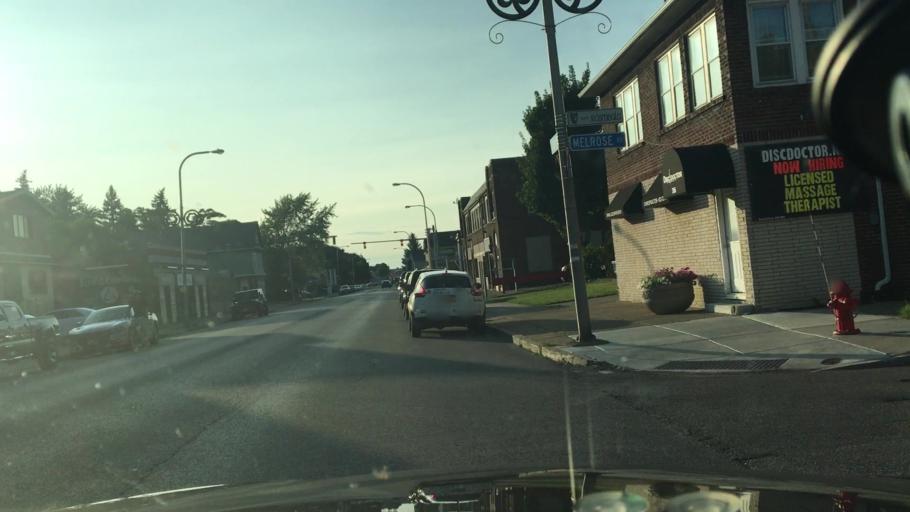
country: US
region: New York
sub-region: Erie County
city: West Seneca
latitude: 42.8534
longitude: -78.8192
